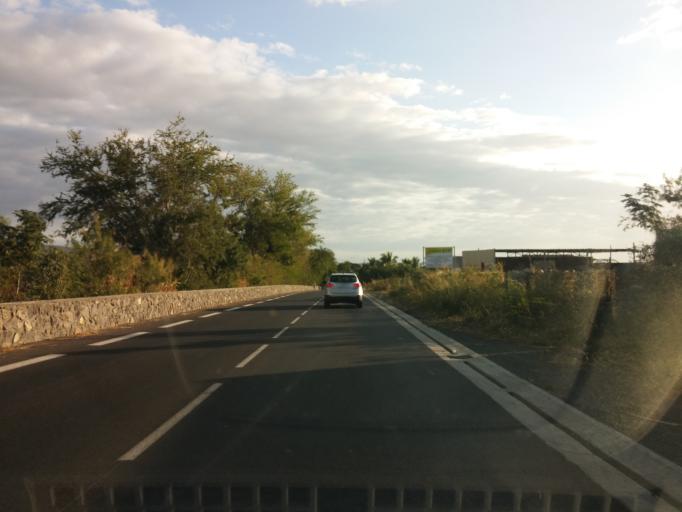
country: RE
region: Reunion
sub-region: Reunion
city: Le Port
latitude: -20.9726
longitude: 55.3072
